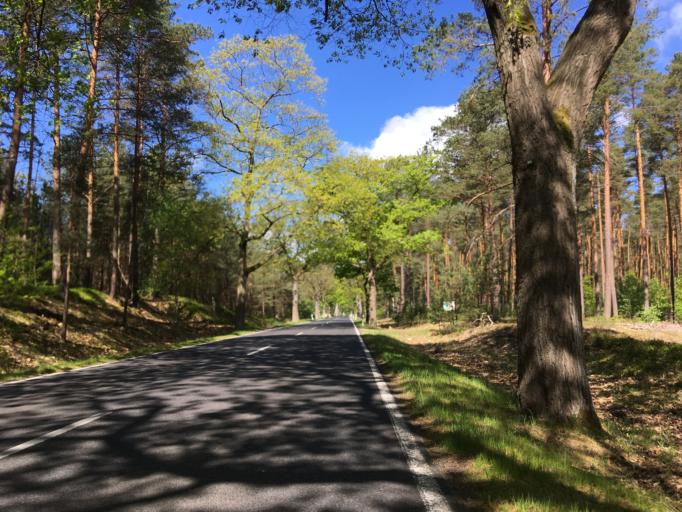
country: DE
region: Brandenburg
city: Birkenwerder
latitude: 52.7229
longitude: 13.3256
